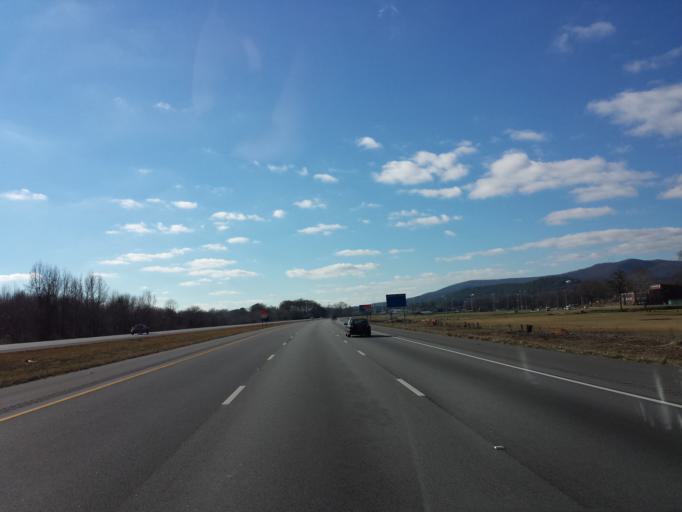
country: US
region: Alabama
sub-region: Calhoun County
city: Oxford
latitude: 33.6059
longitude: -85.8122
